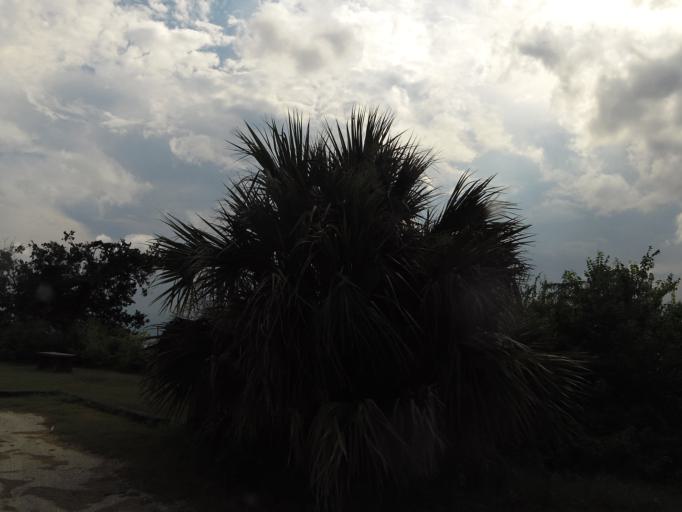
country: US
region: Florida
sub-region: Nassau County
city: Fernandina Beach
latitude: 30.6891
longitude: -81.4569
